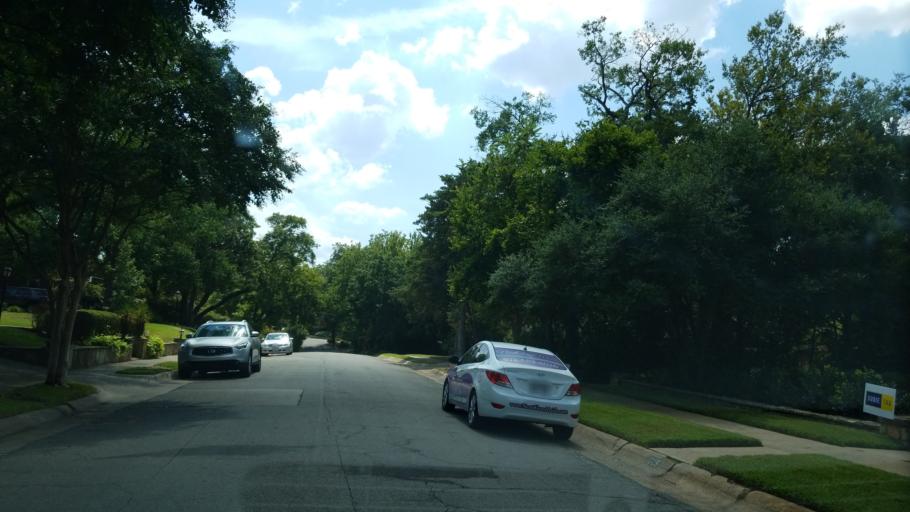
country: US
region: Texas
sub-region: Dallas County
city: Dallas
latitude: 32.7574
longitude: -96.8452
